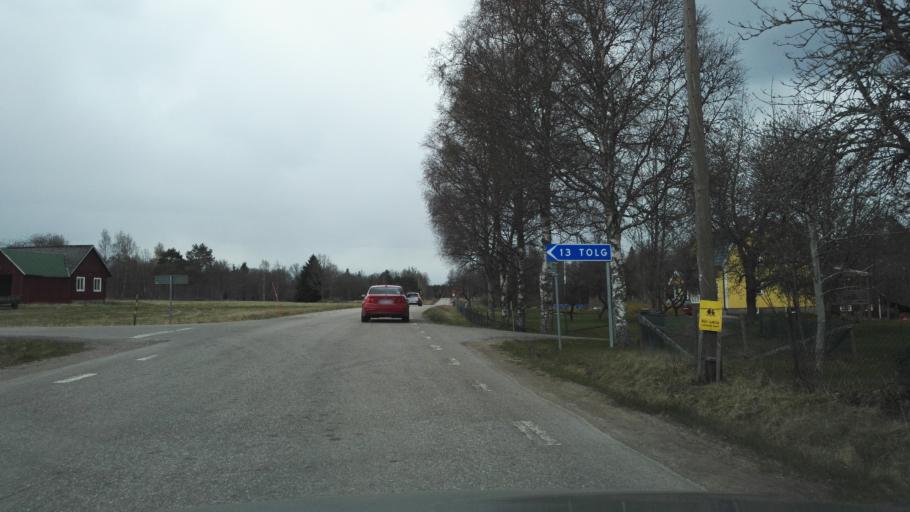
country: SE
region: Kronoberg
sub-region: Vaxjo Kommun
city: Braas
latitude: 57.1124
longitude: 14.9776
